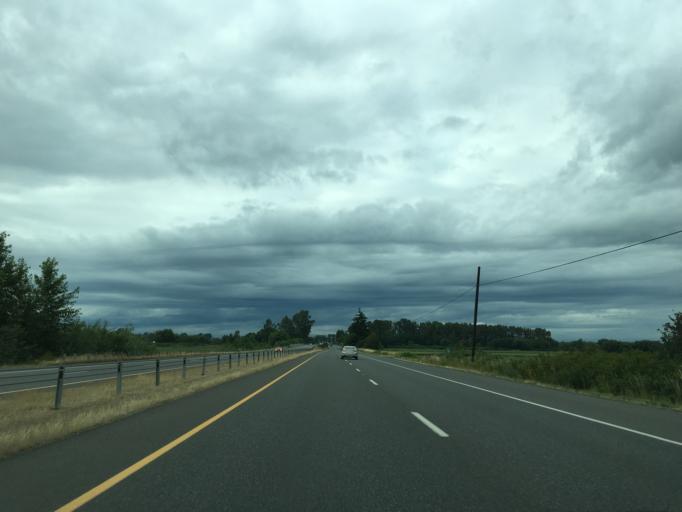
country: US
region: Washington
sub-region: Whatcom County
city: Lynden
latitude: 48.9124
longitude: -122.4856
